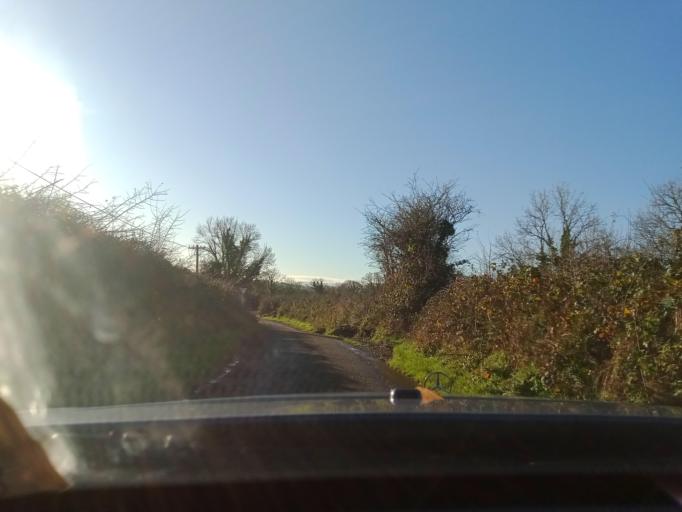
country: IE
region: Munster
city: Carrick-on-Suir
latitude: 52.4437
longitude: -7.4192
